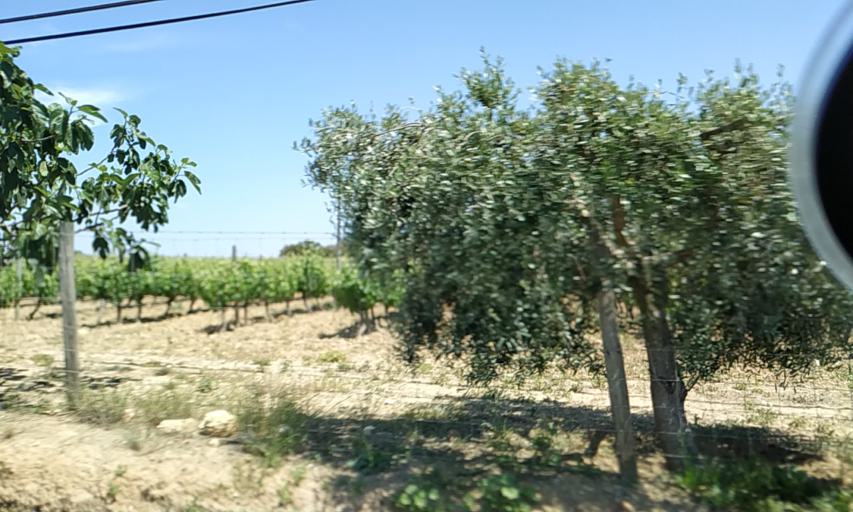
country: PT
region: Santarem
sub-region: Benavente
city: Poceirao
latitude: 38.6626
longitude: -8.7385
